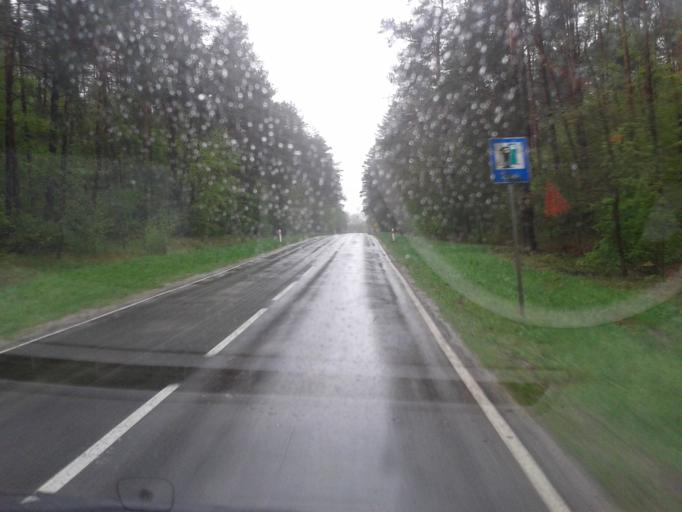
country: PL
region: Subcarpathian Voivodeship
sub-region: Powiat lubaczowski
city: Cieszanow
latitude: 50.2703
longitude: 23.1491
